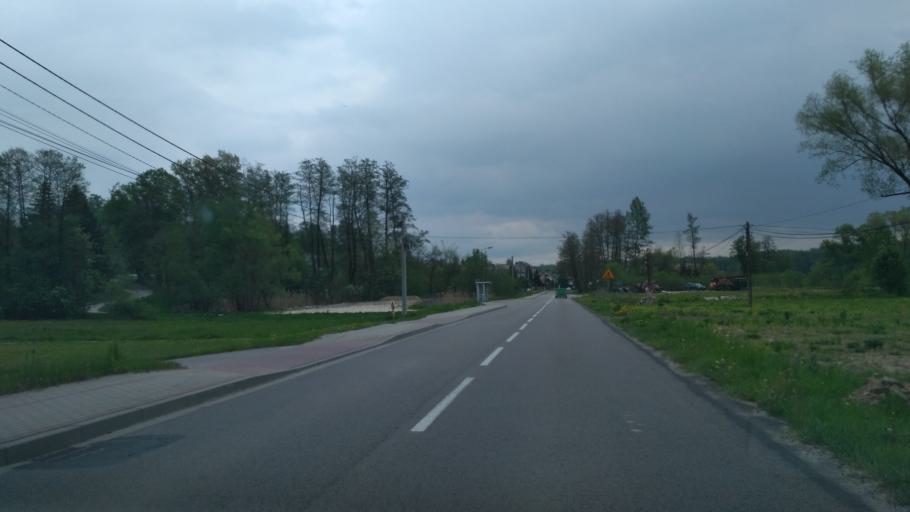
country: PL
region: Lesser Poland Voivodeship
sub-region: Powiat tarnowski
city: Skrzyszow
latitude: 49.9893
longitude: 21.0804
